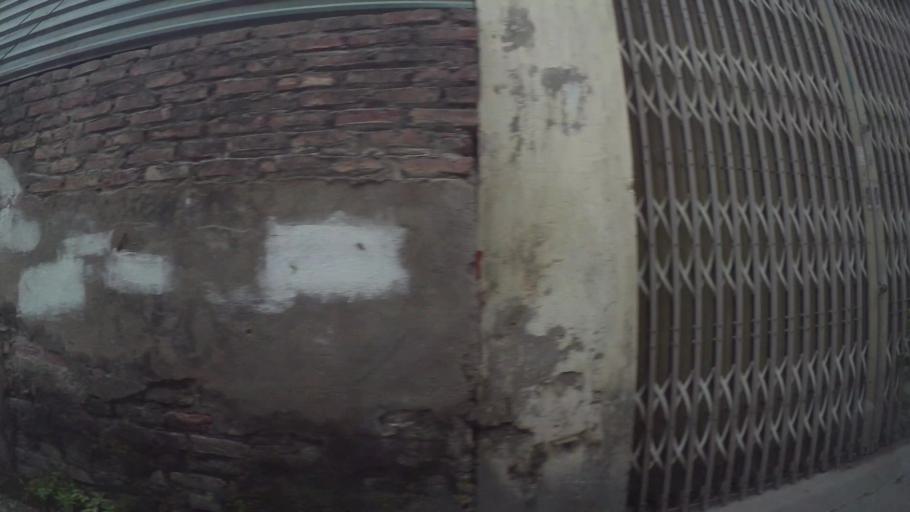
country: VN
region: Ha Noi
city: Hai BaTrung
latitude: 20.9790
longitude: 105.8858
